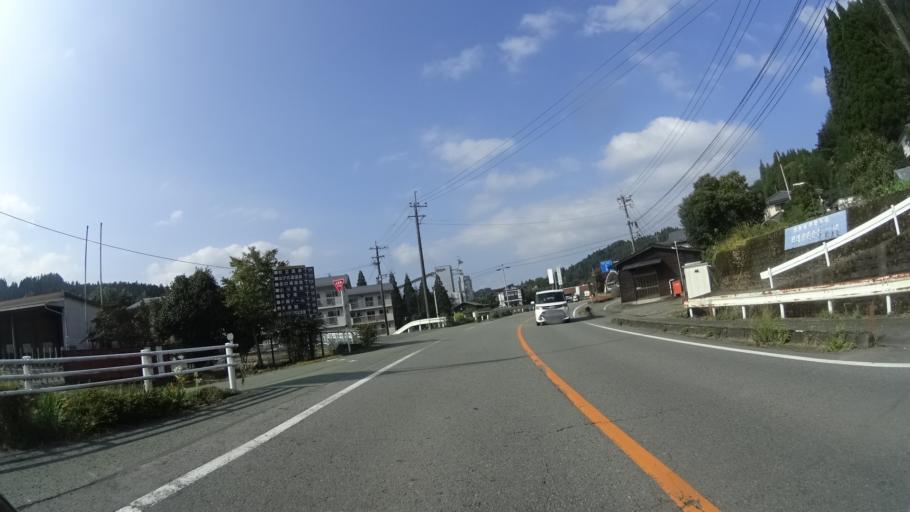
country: JP
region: Kumamoto
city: Aso
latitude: 33.1085
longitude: 131.0639
